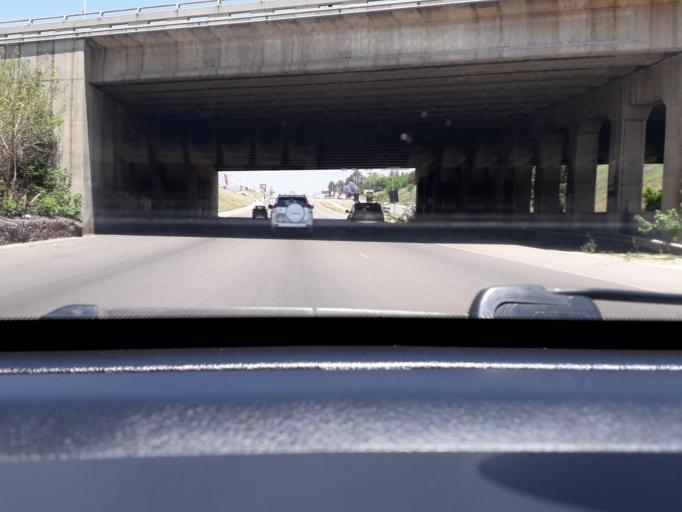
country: ZA
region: Gauteng
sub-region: City of Johannesburg Metropolitan Municipality
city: Midrand
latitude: -26.0438
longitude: 28.0907
